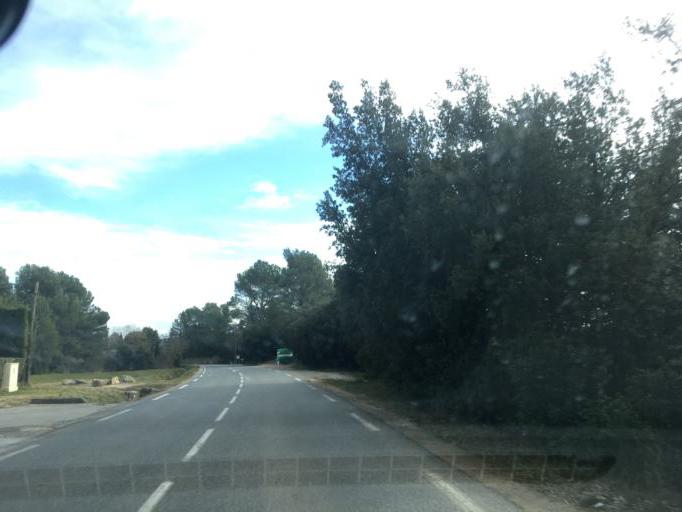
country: FR
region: Provence-Alpes-Cote d'Azur
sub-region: Departement du Var
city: Le Val
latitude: 43.4399
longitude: 6.0586
